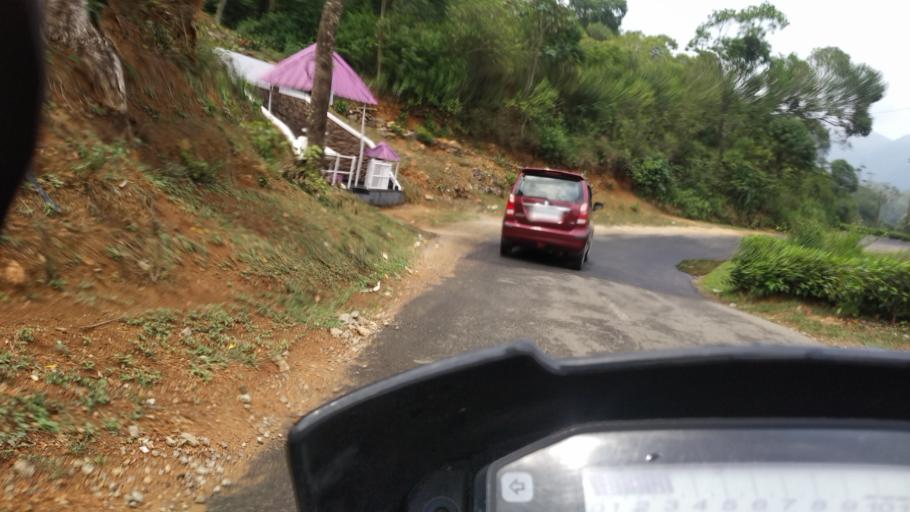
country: IN
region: Kerala
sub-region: Kottayam
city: Erattupetta
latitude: 9.6339
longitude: 76.9588
